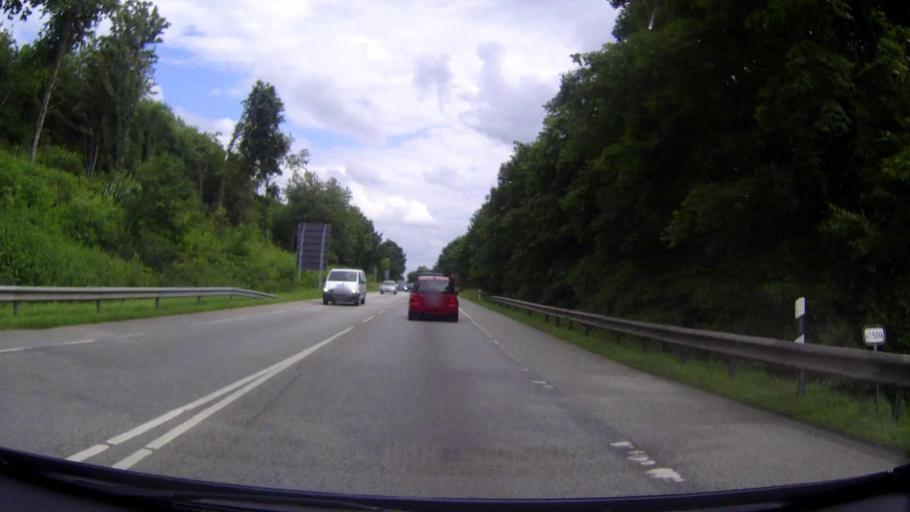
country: DE
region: Schleswig-Holstein
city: Klein Gladebrugge
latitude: 53.9276
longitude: 10.3202
